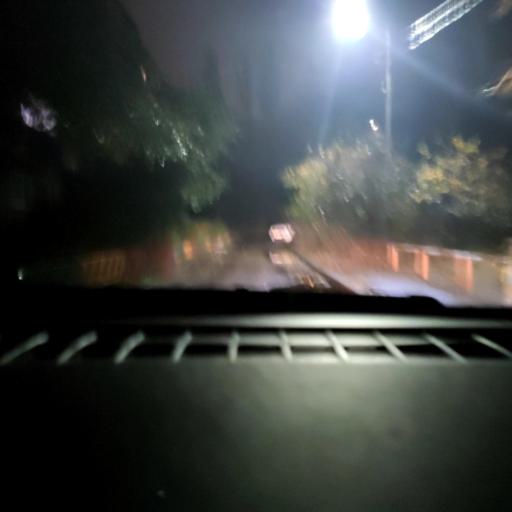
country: RU
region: Voronezj
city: Voronezh
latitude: 51.6474
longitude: 39.1280
